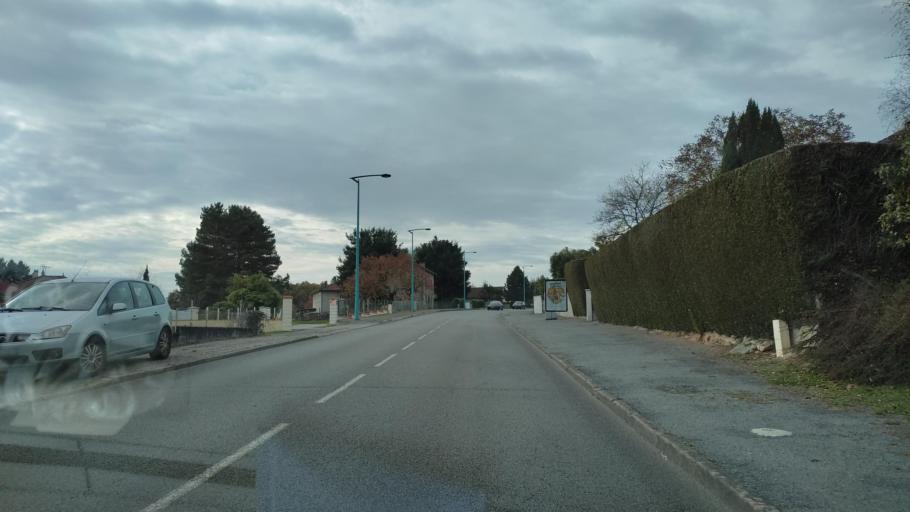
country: FR
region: Limousin
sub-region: Departement de la Haute-Vienne
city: Rilhac-Rancon
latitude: 45.9048
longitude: 1.3256
